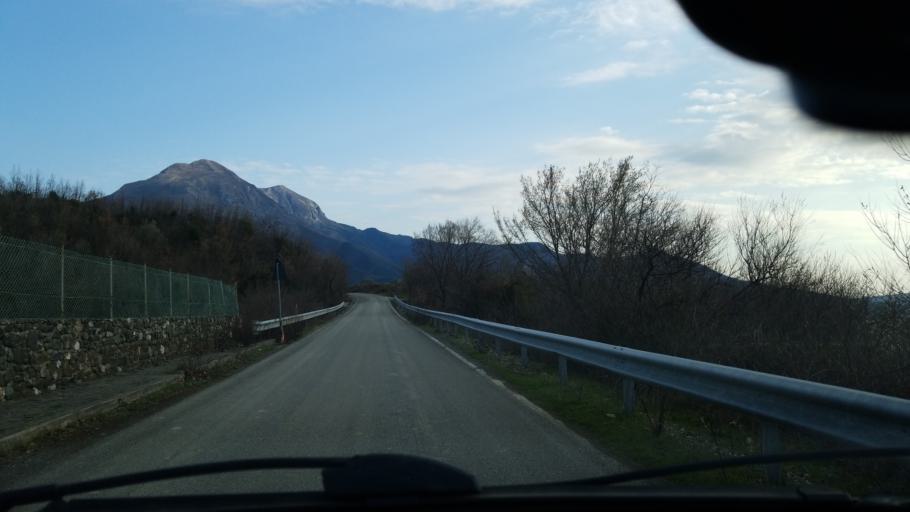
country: AL
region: Lezhe
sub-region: Rrethi i Lezhes
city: Kallmeti i Madh
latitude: 41.8799
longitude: 19.6924
